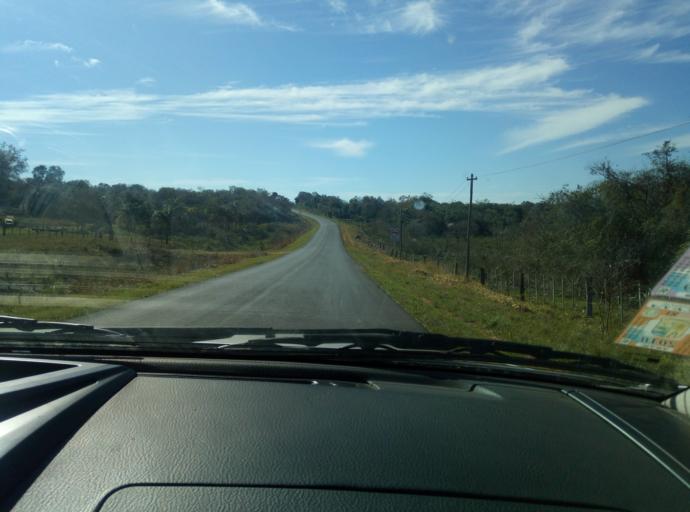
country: PY
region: Caaguazu
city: Carayao
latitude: -25.1731
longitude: -56.3133
